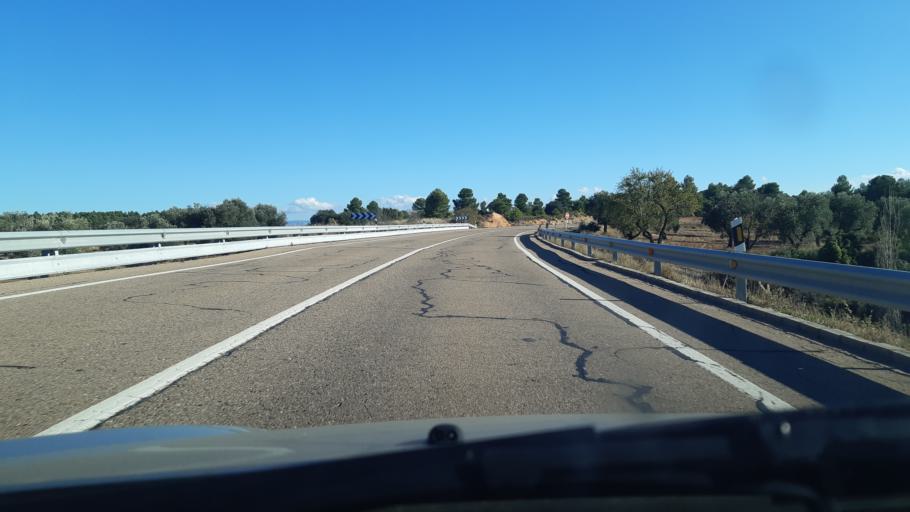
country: ES
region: Aragon
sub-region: Provincia de Teruel
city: Valjunquera
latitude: 40.9516
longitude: -0.0120
